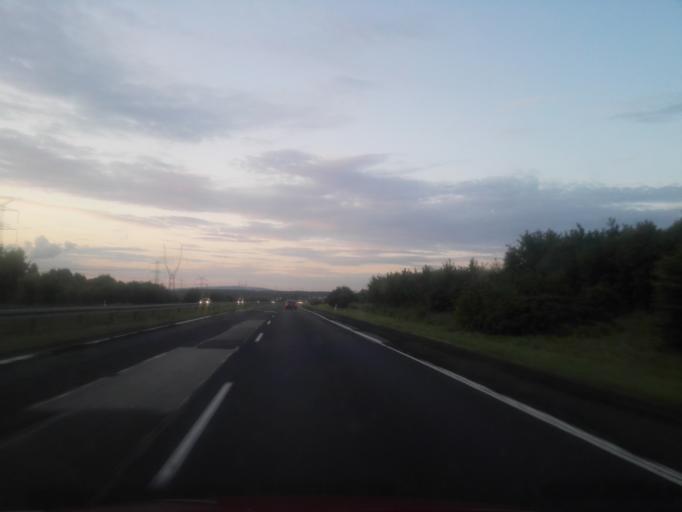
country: PL
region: Lodz Voivodeship
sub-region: Powiat radomszczanski
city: Radomsko
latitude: 51.0931
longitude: 19.3783
